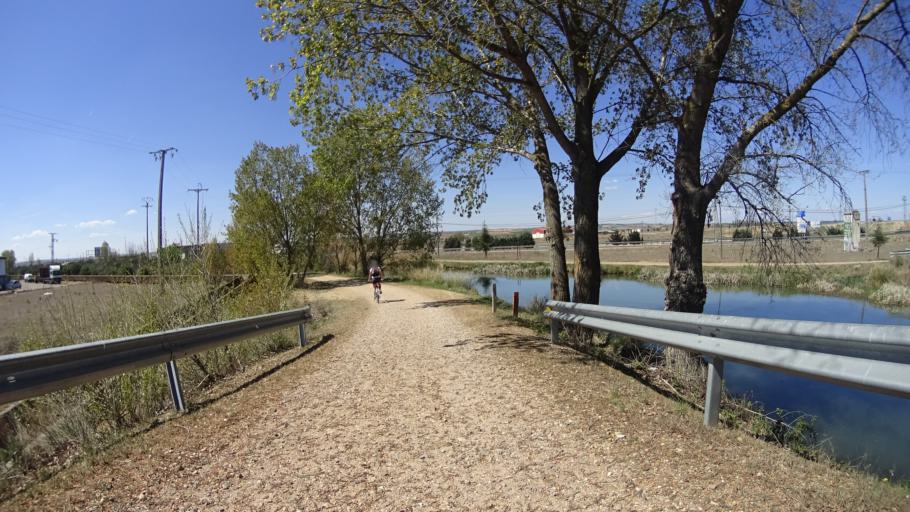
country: ES
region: Castille and Leon
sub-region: Provincia de Valladolid
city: Cabezon
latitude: 41.7542
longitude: -4.6371
